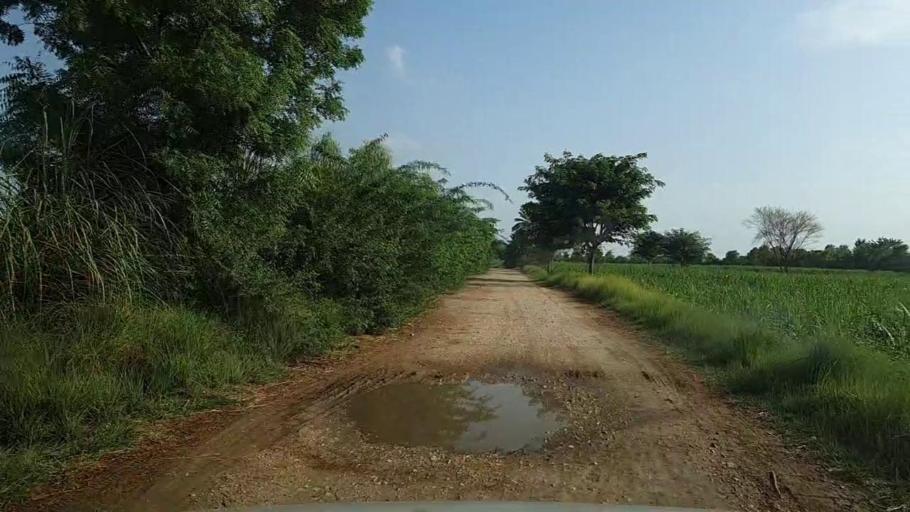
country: PK
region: Sindh
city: Bhiria
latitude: 26.8379
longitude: 68.2410
